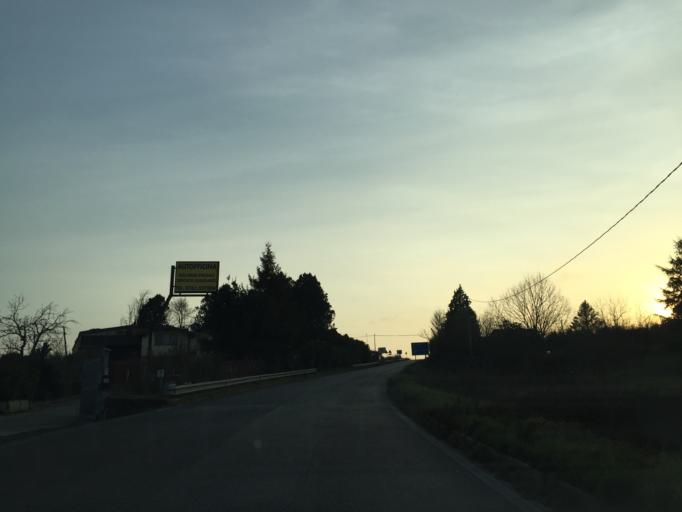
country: IT
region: Latium
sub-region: Citta metropolitana di Roma Capitale
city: Campagnano di Roma
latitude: 42.1614
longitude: 12.3422
